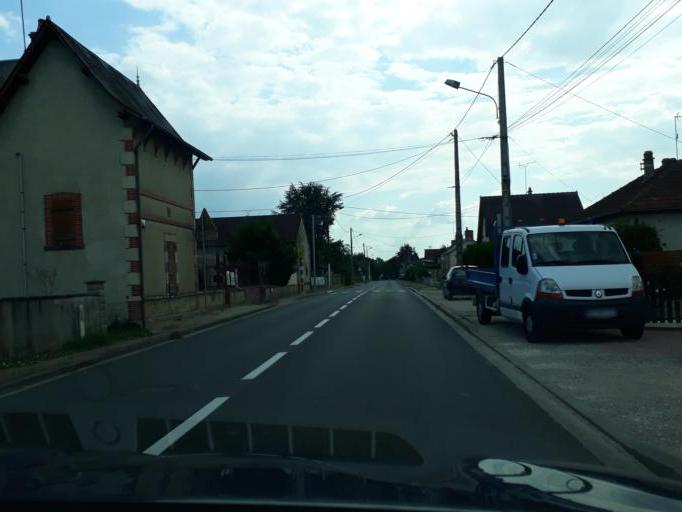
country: FR
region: Centre
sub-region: Departement du Cher
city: Jouet-sur-l'Aubois
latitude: 46.9572
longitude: 2.9562
